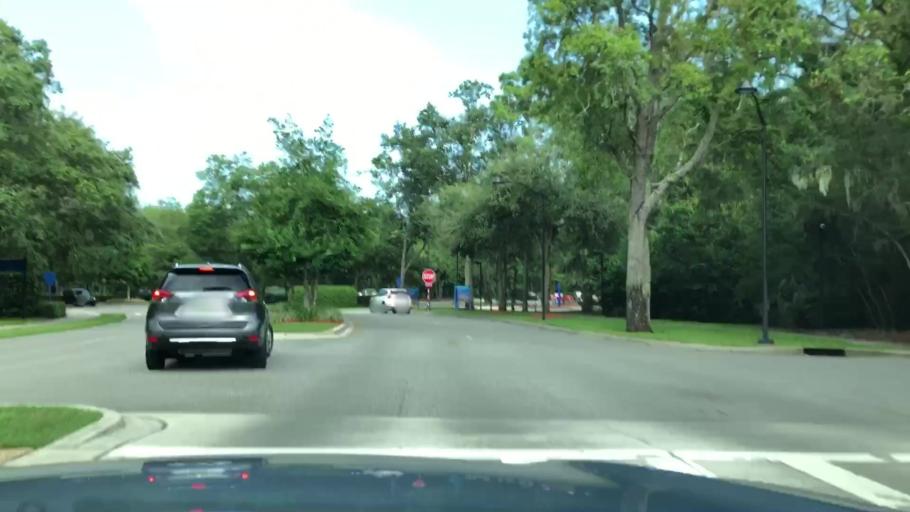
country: US
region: Florida
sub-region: Duval County
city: Jacksonville Beach
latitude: 30.2616
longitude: -81.4403
